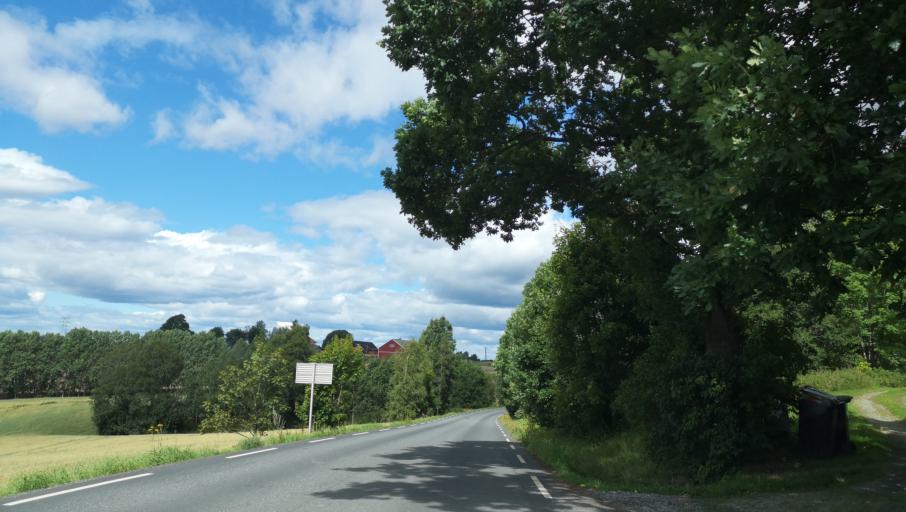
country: NO
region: Akershus
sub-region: Ski
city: Ski
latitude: 59.6936
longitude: 10.8968
